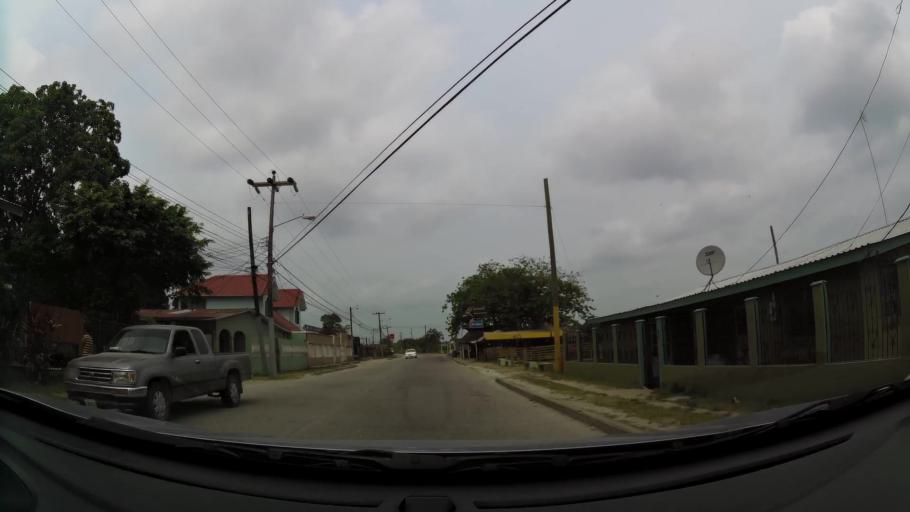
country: HN
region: Atlantida
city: Tela
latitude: 15.7731
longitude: -87.4782
